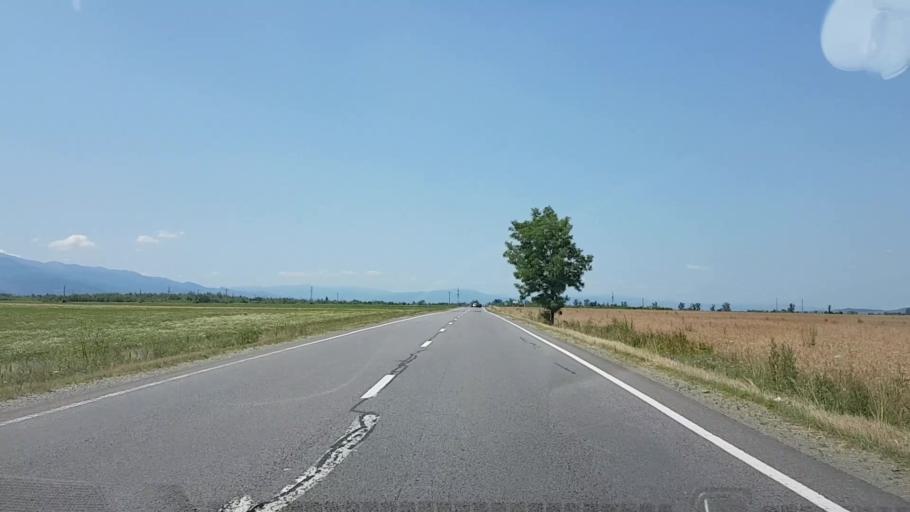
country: RO
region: Sibiu
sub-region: Comuna Arpasu de Jos
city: Arpasu de Jos
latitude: 45.7758
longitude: 24.6103
